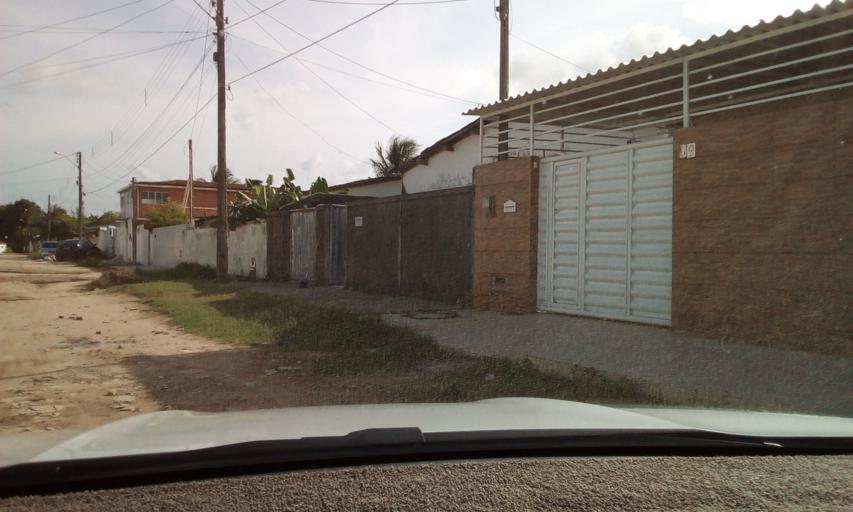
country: BR
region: Paraiba
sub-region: Joao Pessoa
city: Joao Pessoa
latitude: -7.1830
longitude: -34.8245
